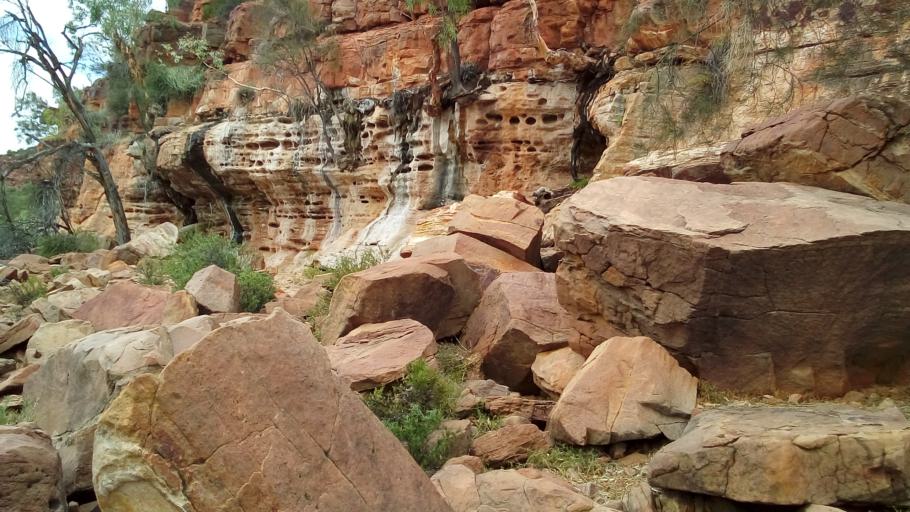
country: AU
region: Western Australia
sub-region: Northampton Shire
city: Kalbarri
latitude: -27.8130
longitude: 114.4748
